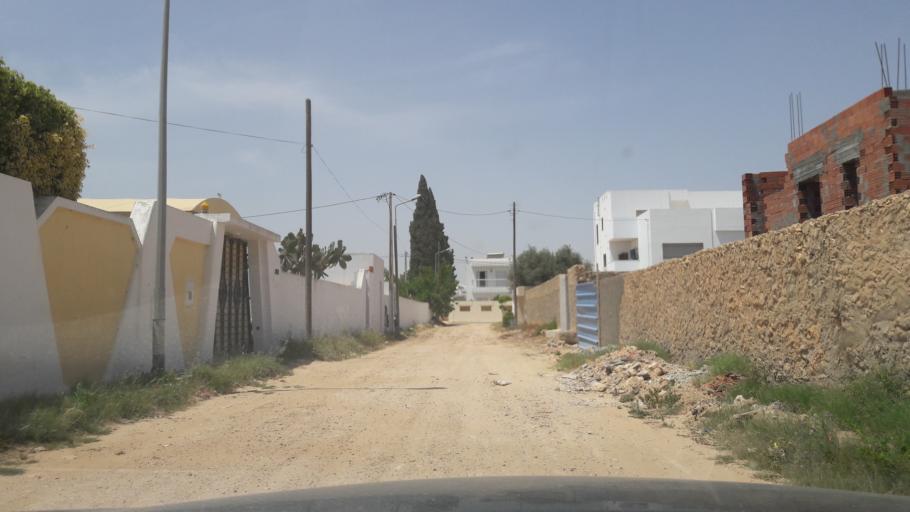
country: TN
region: Safaqis
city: Sfax
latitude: 34.7758
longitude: 10.7548
